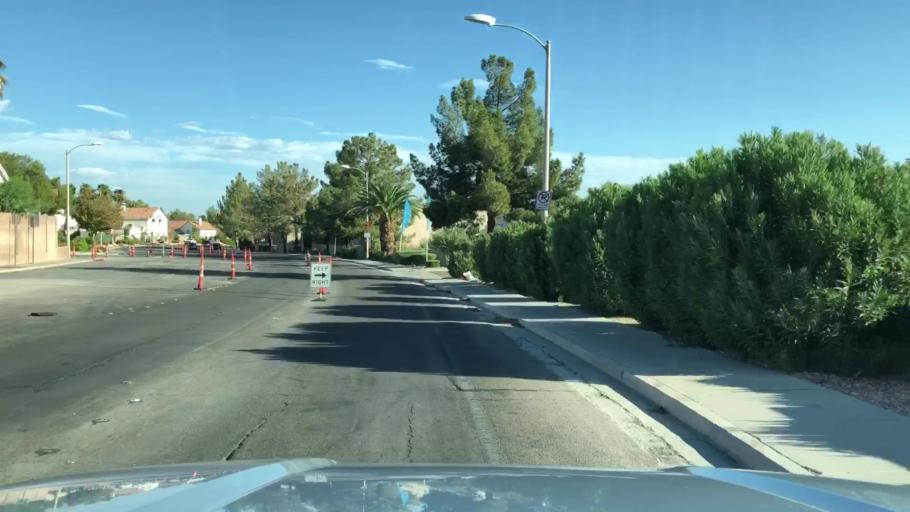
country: US
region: Nevada
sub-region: Clark County
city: Whitney
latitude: 36.0517
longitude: -115.0553
